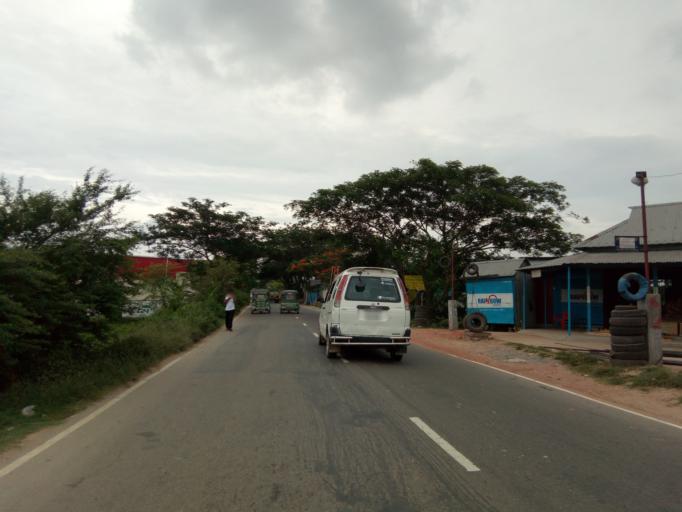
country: BD
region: Dhaka
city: Paltan
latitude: 23.7395
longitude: 90.4804
